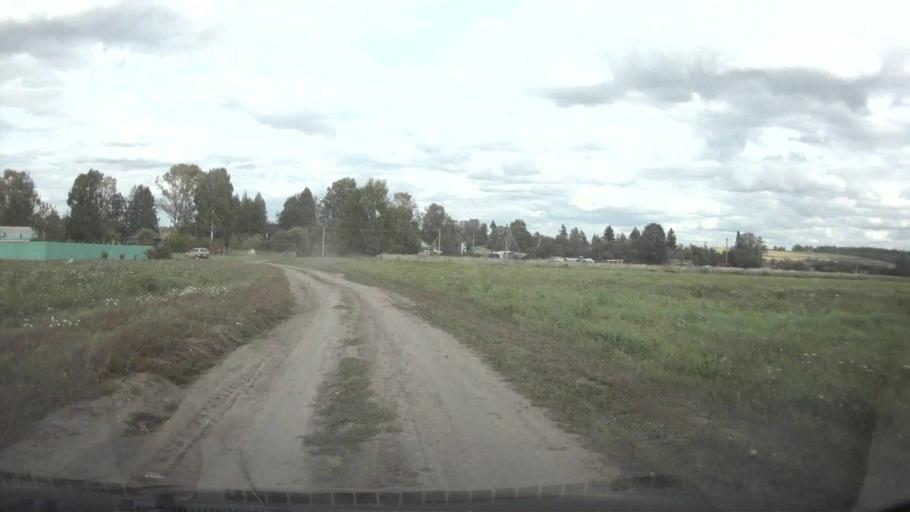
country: RU
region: Mariy-El
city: Kuzhener
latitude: 56.9745
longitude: 48.7958
